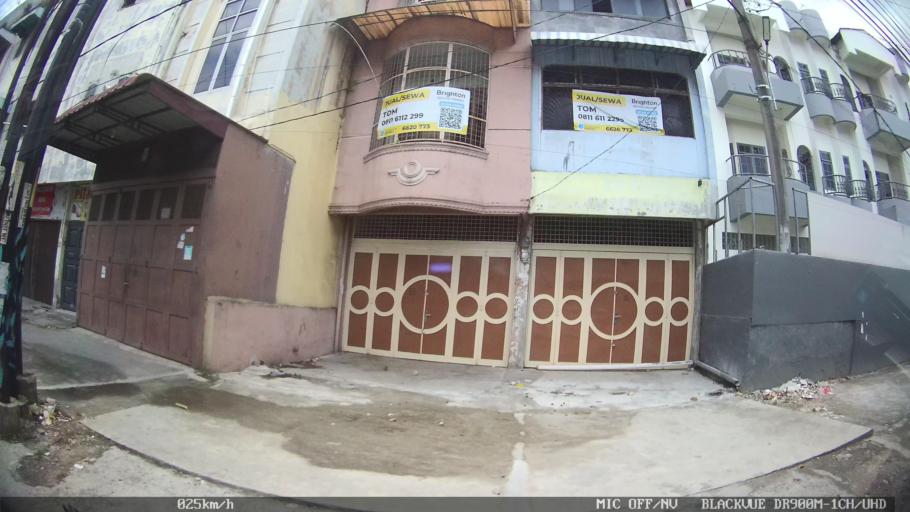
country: ID
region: North Sumatra
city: Medan
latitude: 3.6268
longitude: 98.6682
